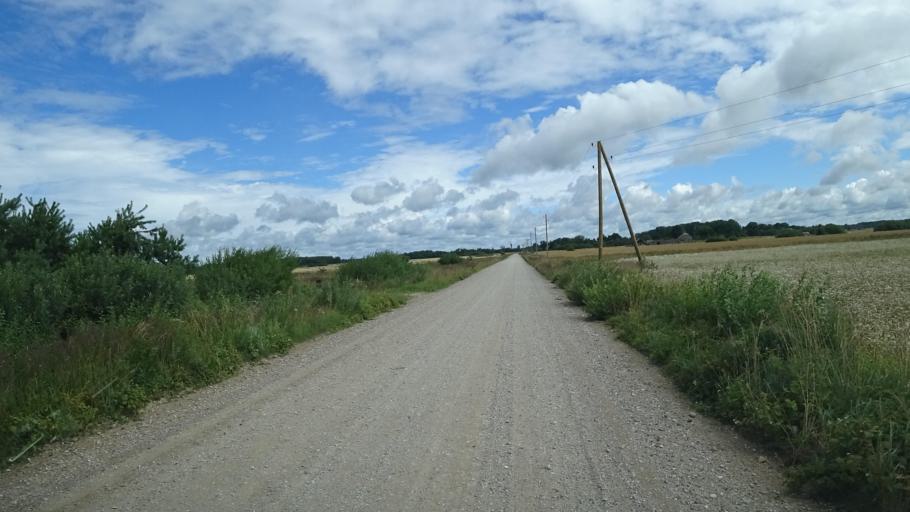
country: LV
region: Liepaja
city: Vec-Liepaja
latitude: 56.6513
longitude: 21.0499
